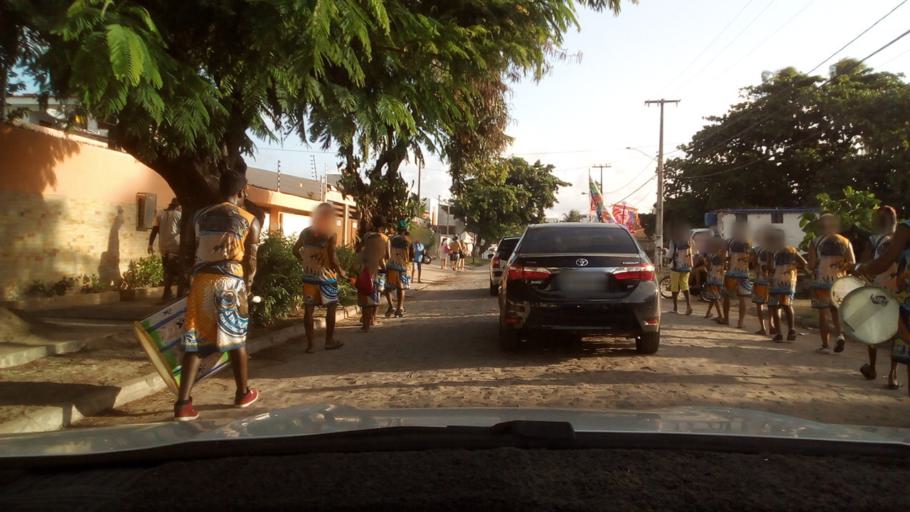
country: BR
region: Paraiba
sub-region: Cabedelo
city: Cabedelo
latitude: -7.0190
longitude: -34.8302
